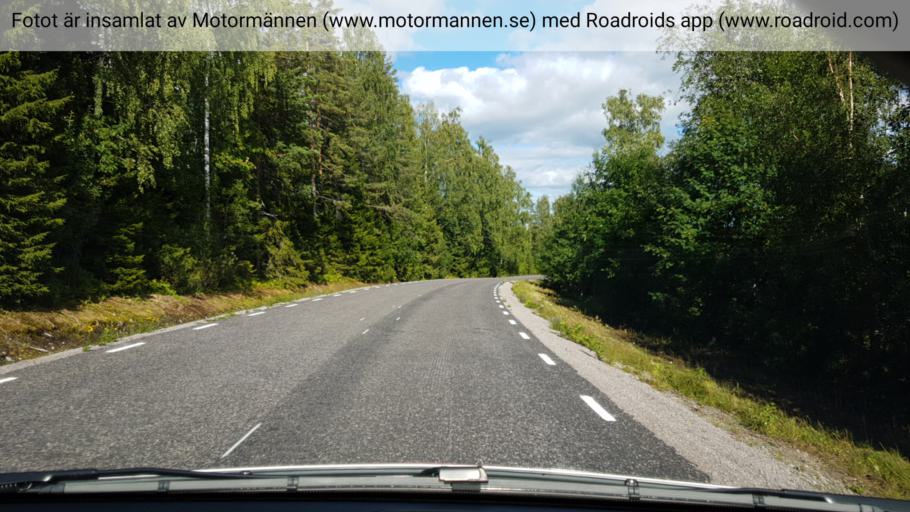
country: SE
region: Vaesterbotten
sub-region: Umea Kommun
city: Hoernefors
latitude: 63.7011
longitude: 19.7800
